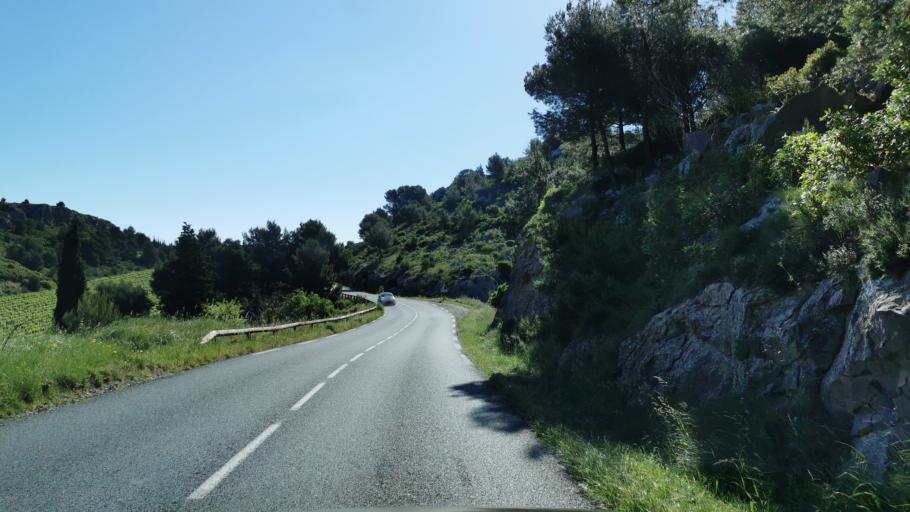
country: FR
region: Languedoc-Roussillon
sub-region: Departement de l'Aude
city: Armissan
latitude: 43.1765
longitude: 3.0949
